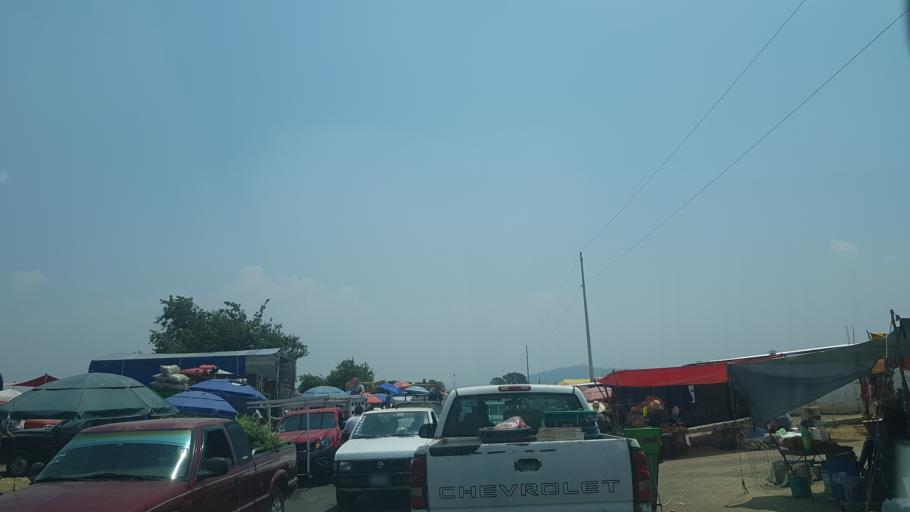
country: MX
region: Puebla
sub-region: San Jeronimo Tecuanipan
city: San Miguel Papaxtla
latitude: 19.0967
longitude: -98.4144
